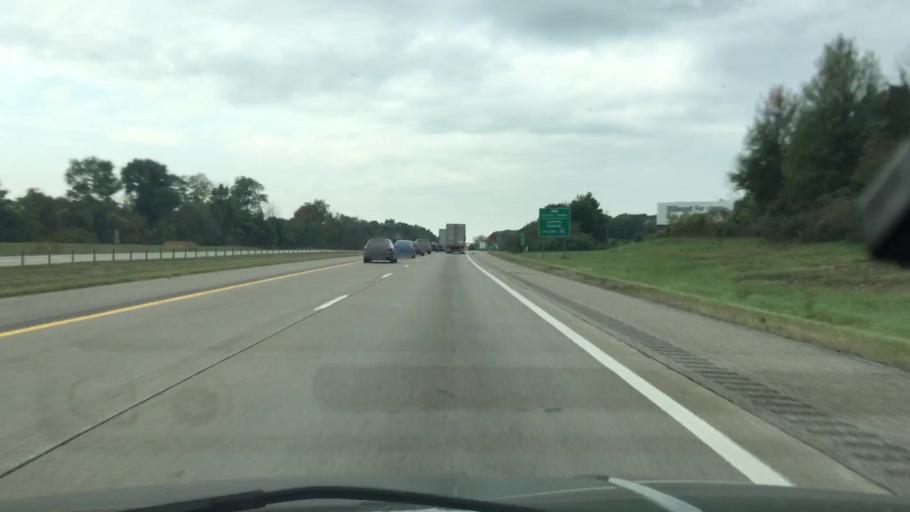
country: US
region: Michigan
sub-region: Berrien County
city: Benton Heights
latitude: 42.1452
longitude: -86.3531
